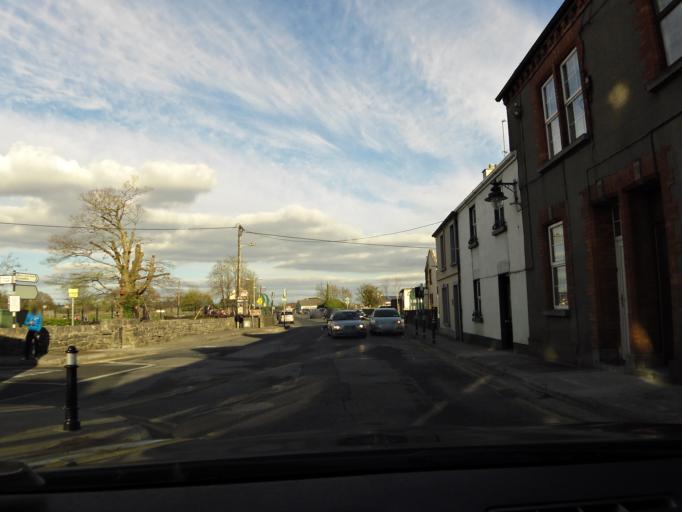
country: IE
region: Connaught
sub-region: County Galway
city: Athenry
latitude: 53.2989
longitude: -8.7455
